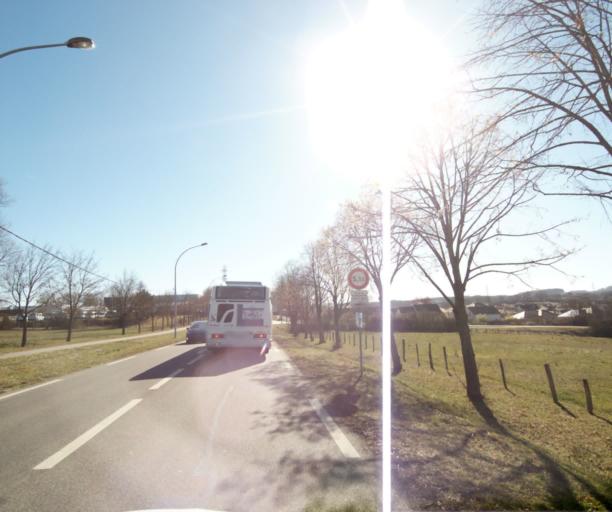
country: FR
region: Lorraine
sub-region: Departement de Meurthe-et-Moselle
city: Heillecourt
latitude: 48.6540
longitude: 6.2072
